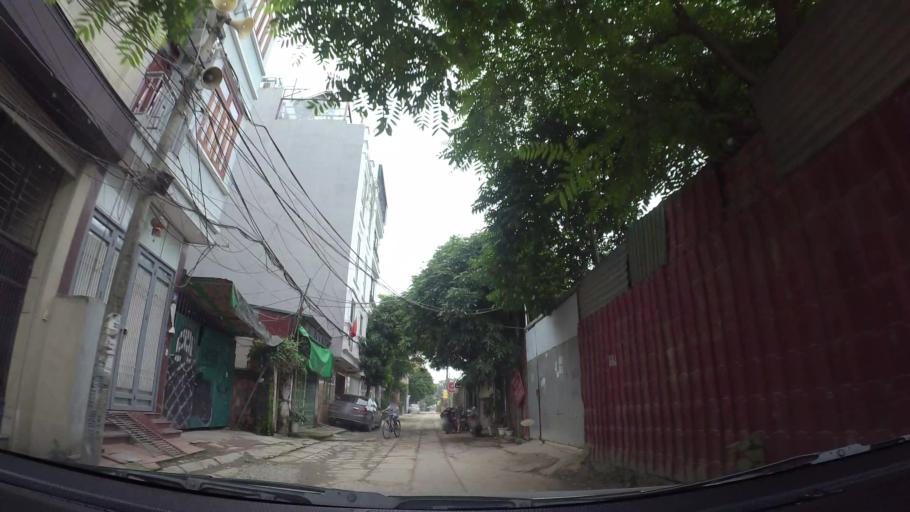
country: VN
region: Ha Noi
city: Tay Ho
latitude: 21.0664
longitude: 105.8364
